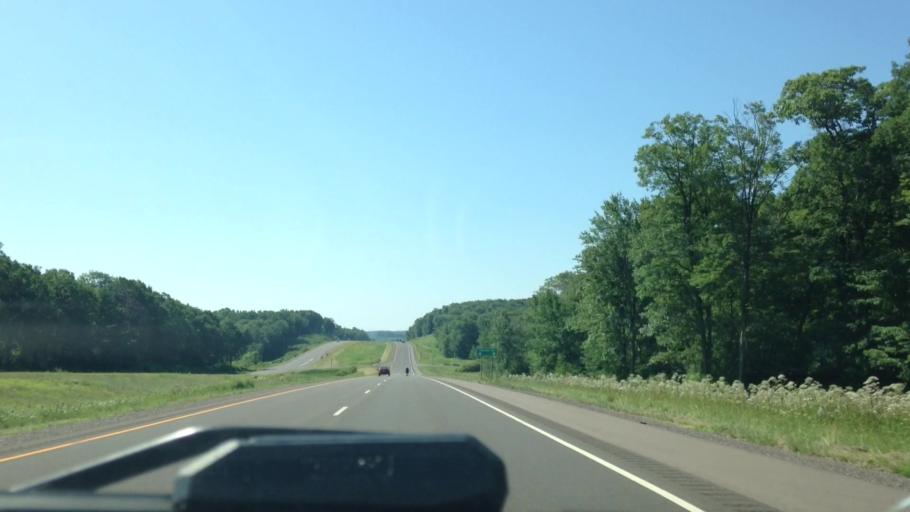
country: US
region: Wisconsin
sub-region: Washburn County
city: Spooner
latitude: 46.0016
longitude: -91.8329
